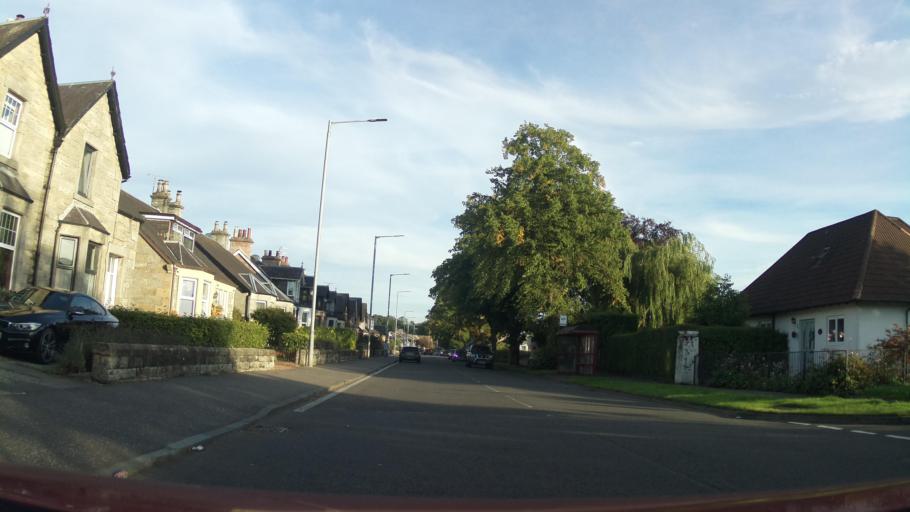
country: GB
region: Scotland
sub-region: Clackmannanshire
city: Alloa
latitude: 56.1226
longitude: -3.8020
